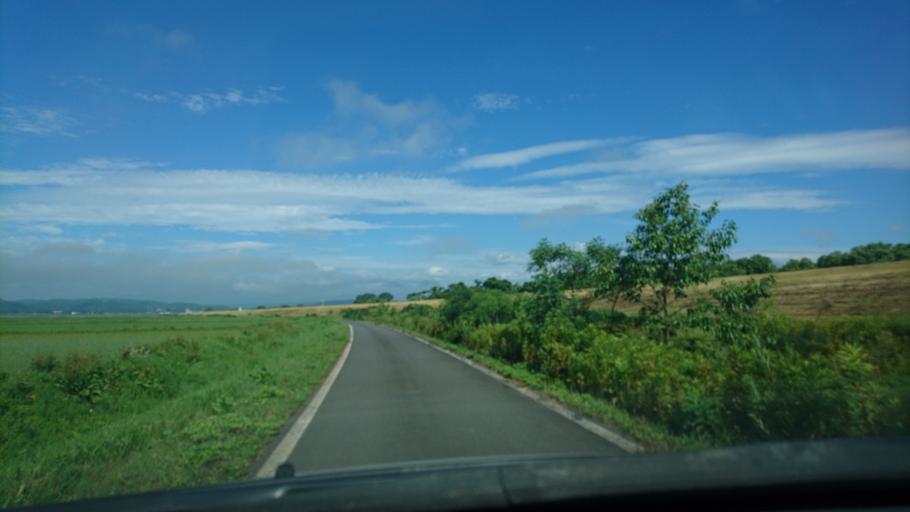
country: JP
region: Iwate
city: Ichinoseki
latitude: 38.9742
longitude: 141.1516
